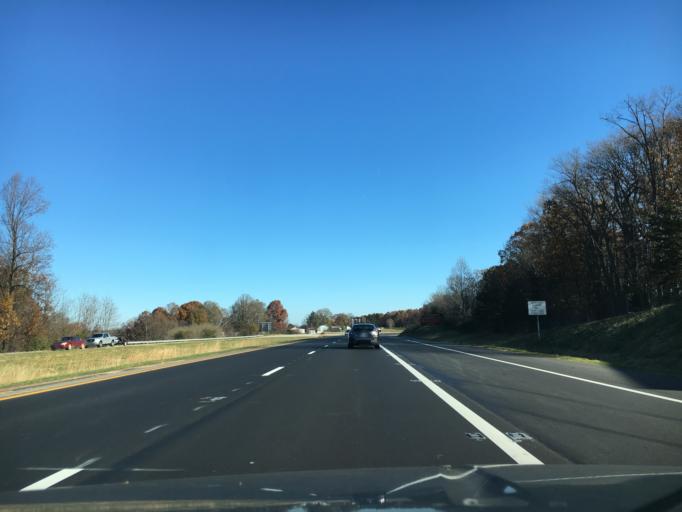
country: US
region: Virginia
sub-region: Appomattox County
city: Appomattox
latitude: 37.3662
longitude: -78.8347
